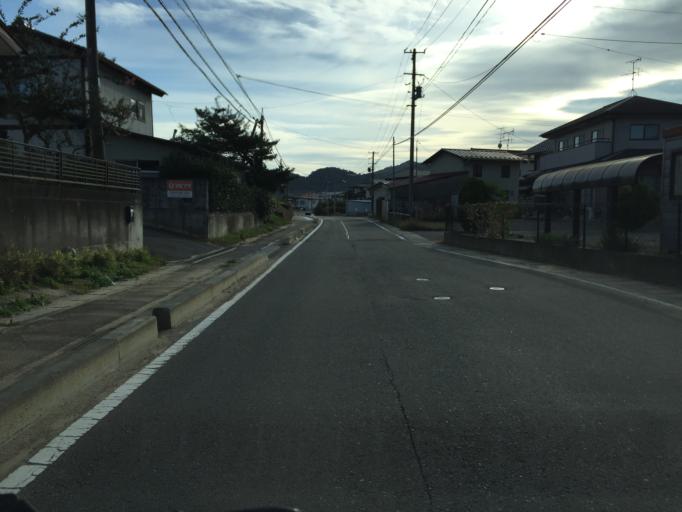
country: JP
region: Fukushima
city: Hobaramachi
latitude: 37.7918
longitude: 140.5994
